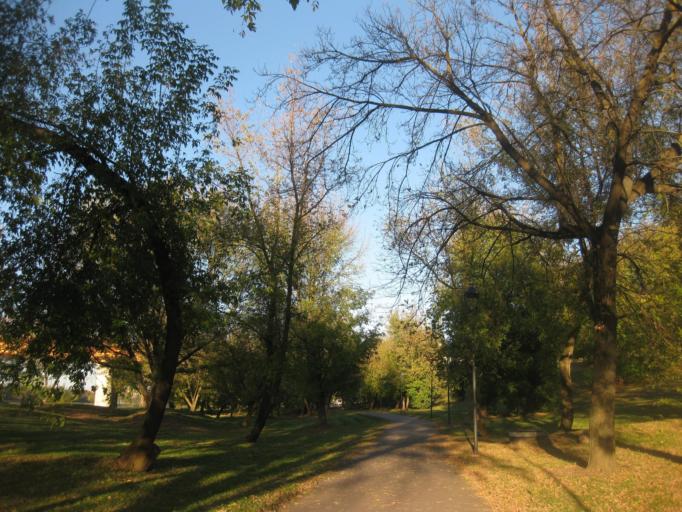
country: LT
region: Kauno apskritis
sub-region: Kaunas
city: Kaunas
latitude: 54.9014
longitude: 23.8911
